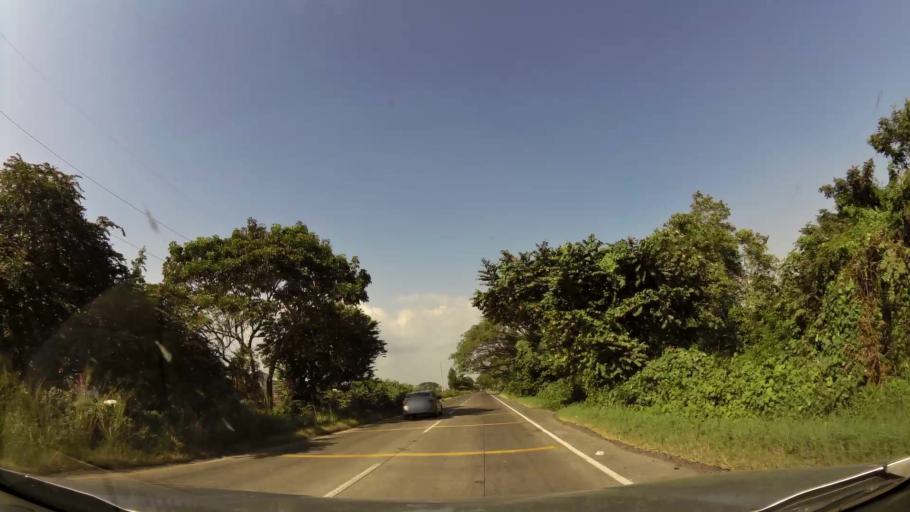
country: GT
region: Escuintla
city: Puerto San Jose
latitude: 13.9686
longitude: -90.7885
